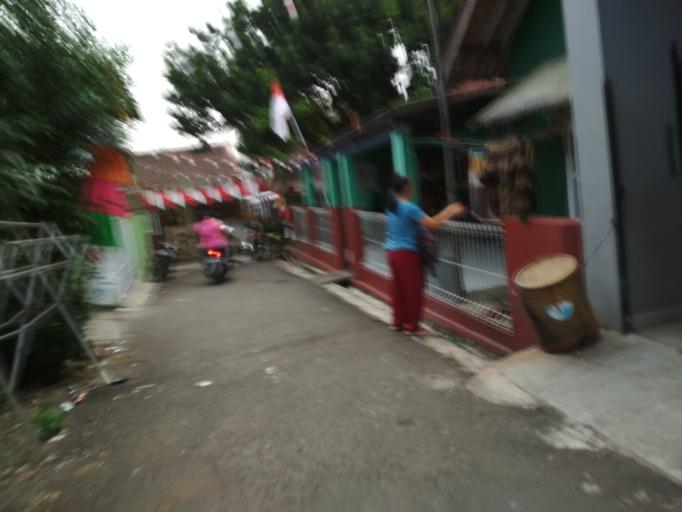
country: ID
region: West Java
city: Ciampea
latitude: -6.5572
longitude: 106.7382
